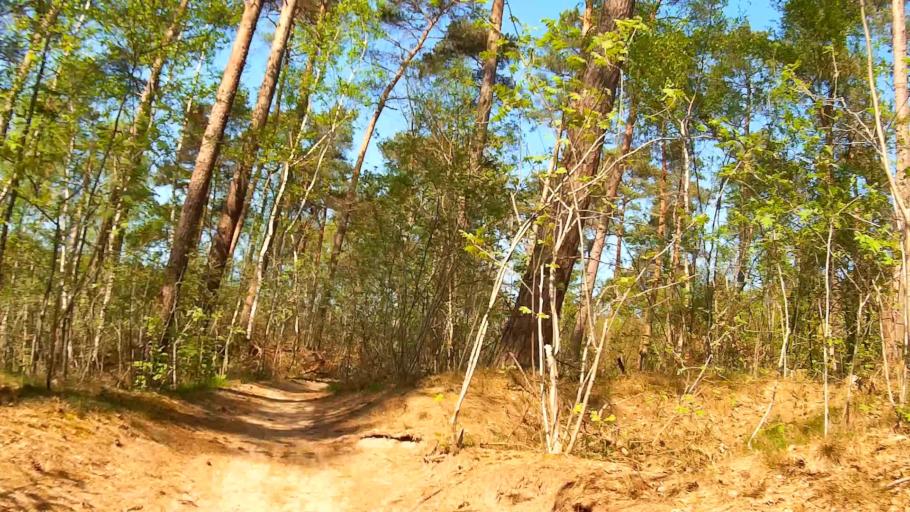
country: NL
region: Utrecht
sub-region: Gemeente Baarn
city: Baarn
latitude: 52.1913
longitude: 5.2535
